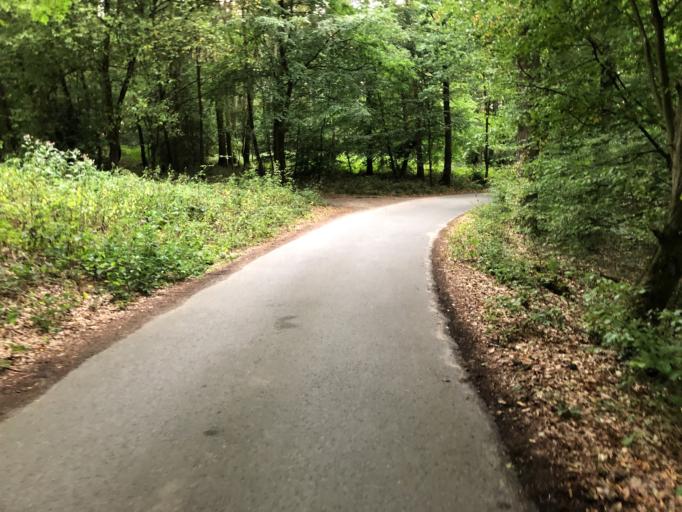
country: DE
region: North Rhine-Westphalia
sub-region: Regierungsbezirk Dusseldorf
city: Muelheim (Ruhr)
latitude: 51.3902
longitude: 6.8862
